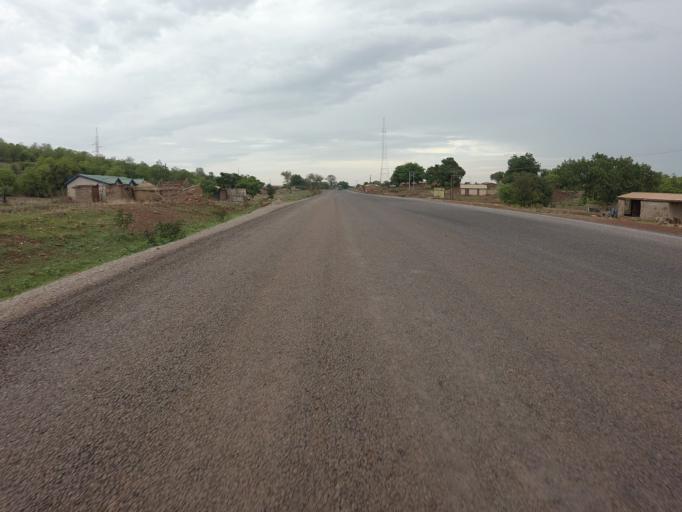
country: GH
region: Upper East
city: Bolgatanga
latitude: 10.8460
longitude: -0.6830
